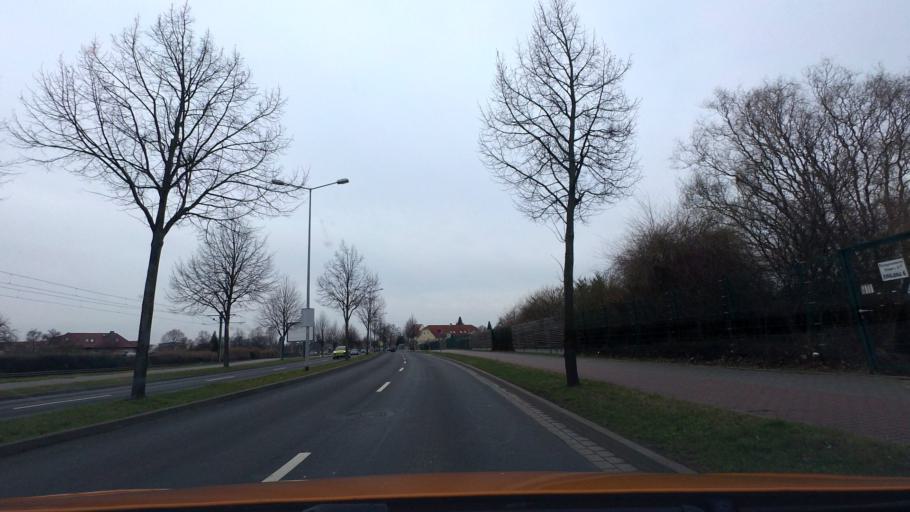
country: DE
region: Saxony-Anhalt
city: Magdeburg
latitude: 52.1402
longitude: 11.5991
